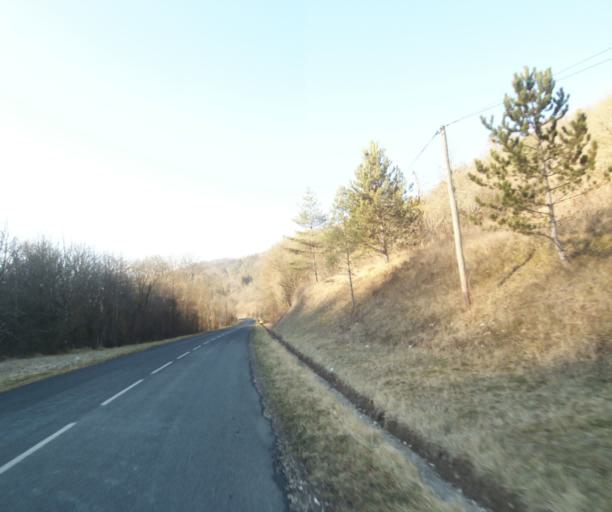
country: FR
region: Champagne-Ardenne
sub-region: Departement de la Haute-Marne
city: Chevillon
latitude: 48.5256
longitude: 5.1596
